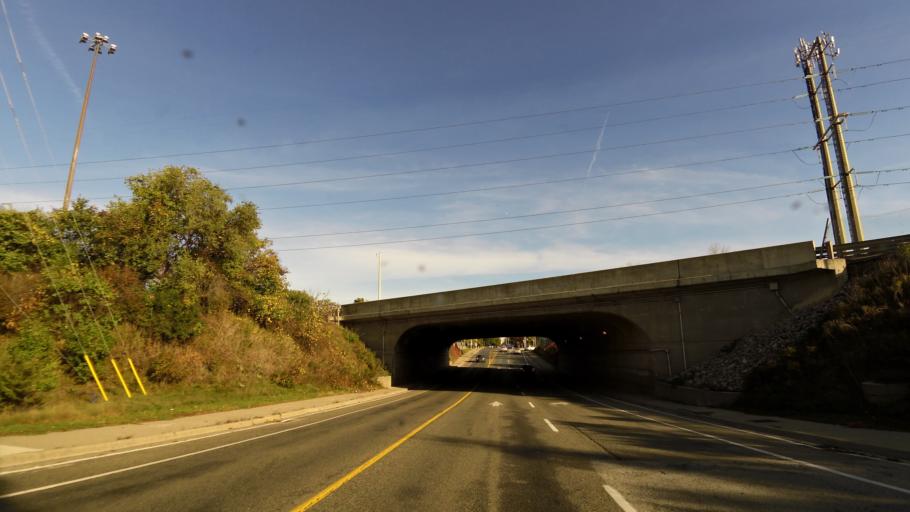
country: CA
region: Ontario
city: Mississauga
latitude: 43.5523
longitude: -79.6145
